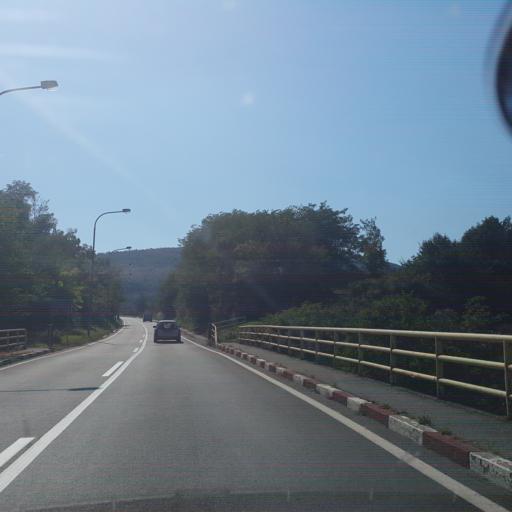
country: RS
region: Central Serbia
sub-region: Zajecarski Okrug
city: Knjazevac
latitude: 43.5500
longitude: 22.2366
